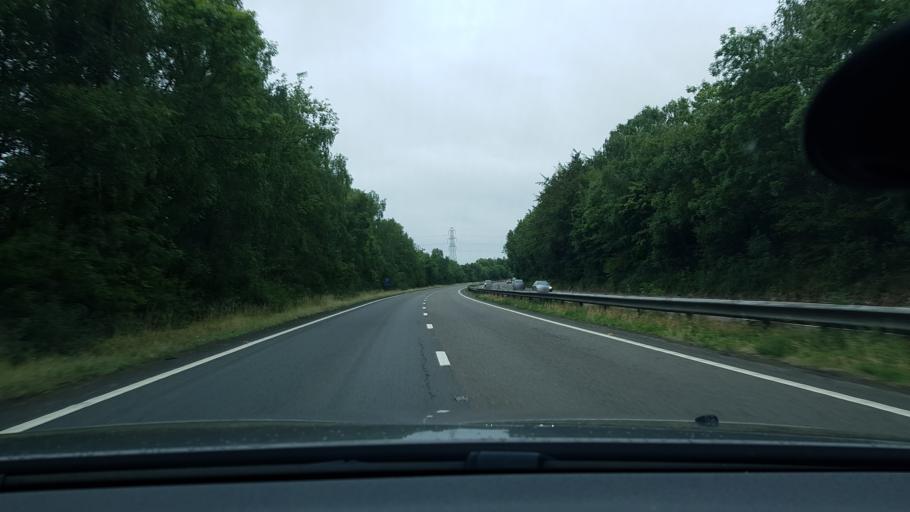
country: GB
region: England
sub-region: Hampshire
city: Overton
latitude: 51.2644
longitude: -1.3392
